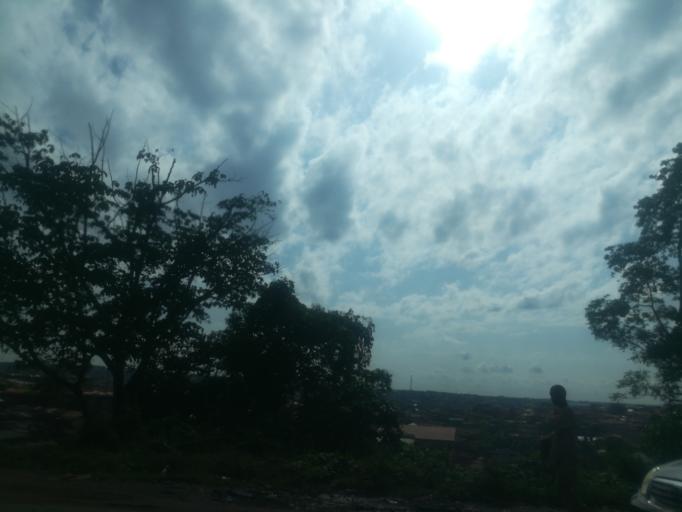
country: NG
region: Oyo
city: Ibadan
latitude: 7.3771
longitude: 3.9302
